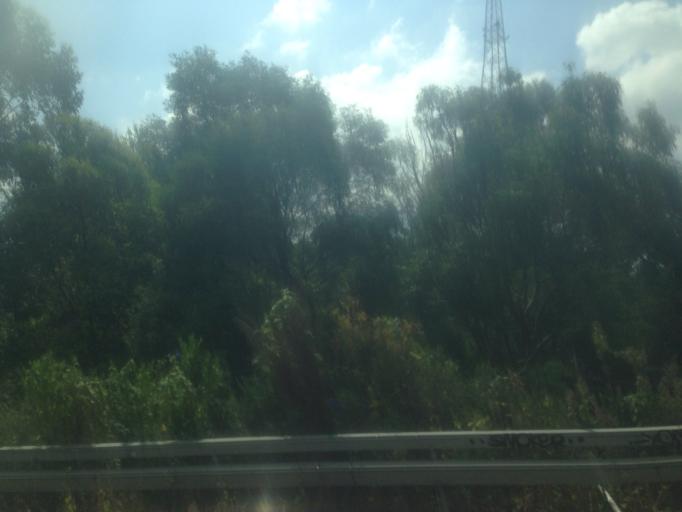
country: AU
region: New South Wales
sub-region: Willoughby
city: Artarmon
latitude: -33.8128
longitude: 151.1921
